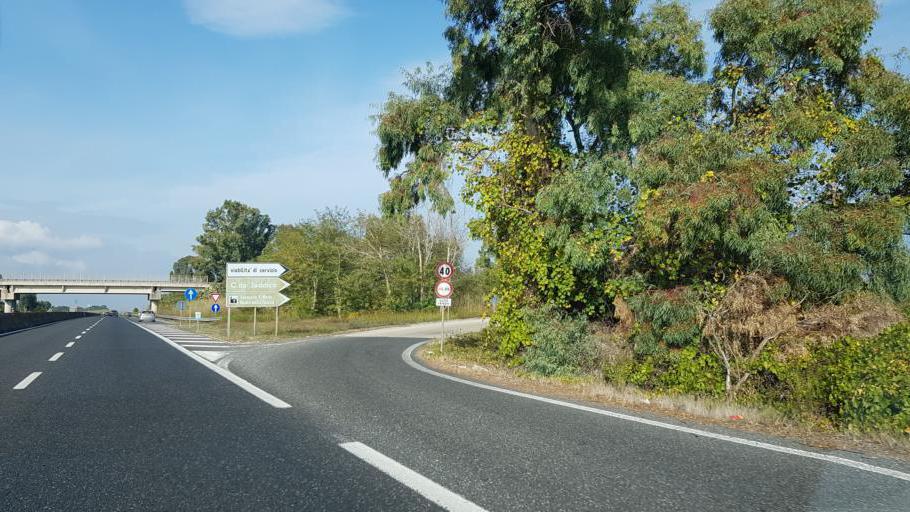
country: IT
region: Apulia
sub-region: Provincia di Brindisi
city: Brindisi
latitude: 40.6647
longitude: 17.8777
